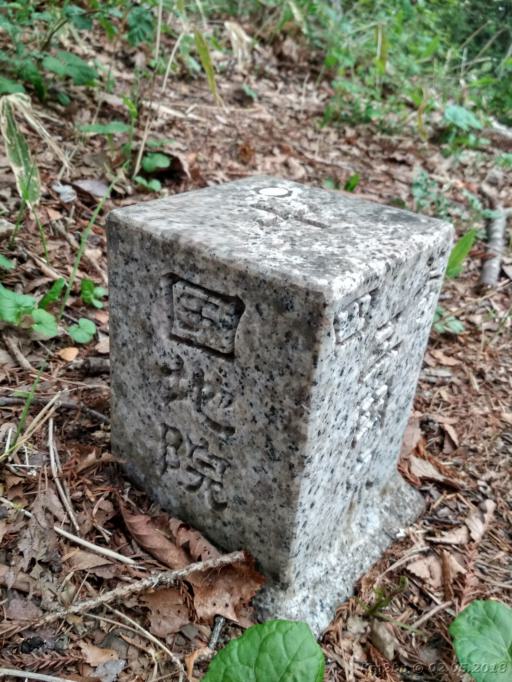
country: JP
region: Yamanashi
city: Fujikawaguchiko
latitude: 35.5033
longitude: 138.7806
